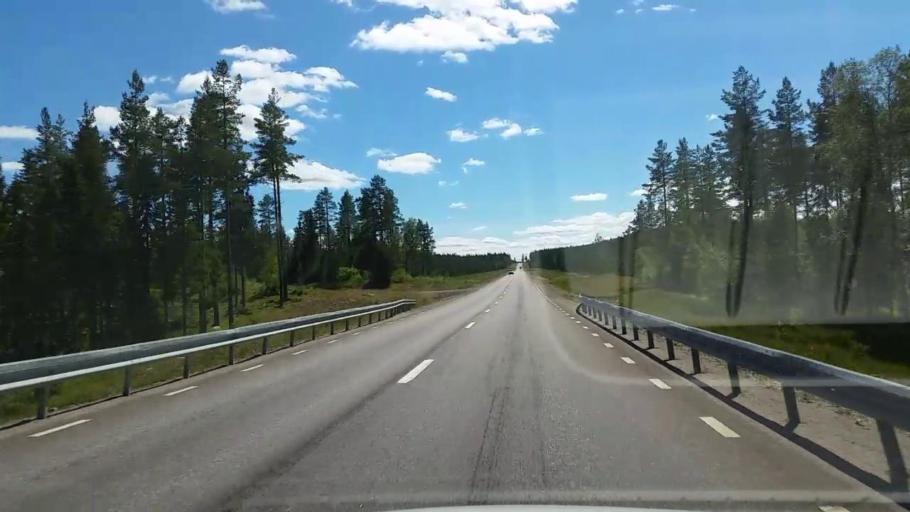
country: SE
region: Gaevleborg
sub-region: Bollnas Kommun
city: Vittsjo
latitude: 61.1210
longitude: 15.8660
